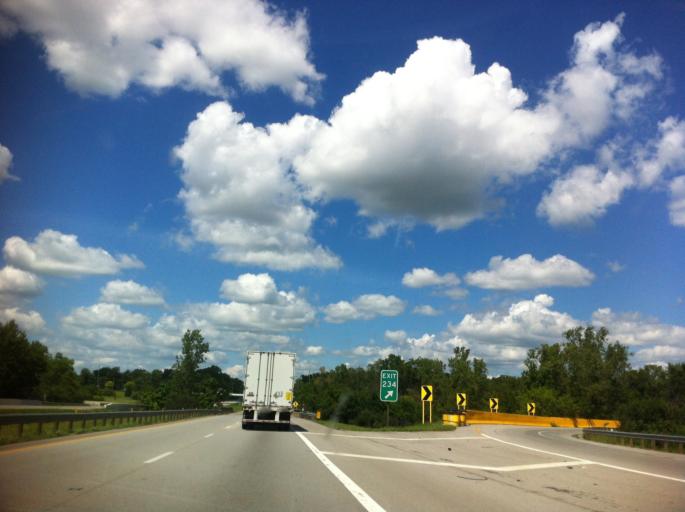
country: US
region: Ohio
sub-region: Lucas County
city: Sylvania
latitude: 41.7108
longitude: -83.6880
